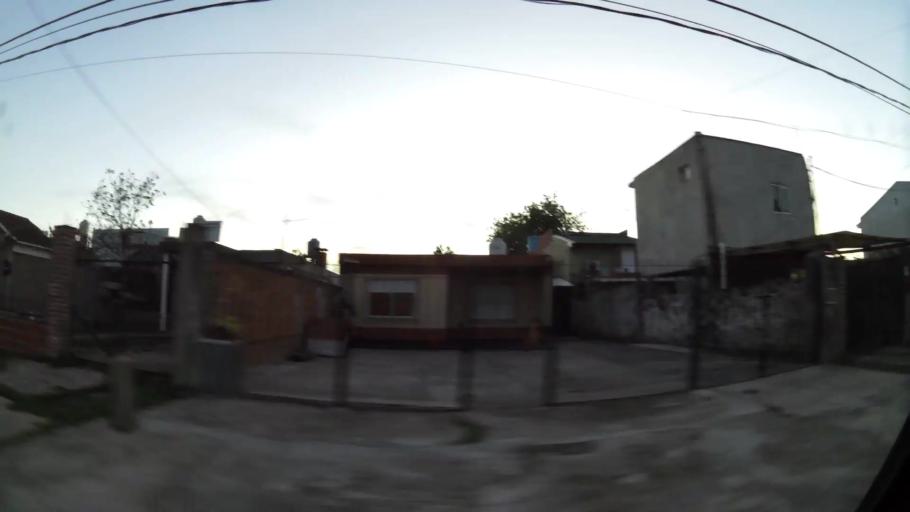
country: AR
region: Buenos Aires
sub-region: Partido de Quilmes
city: Quilmes
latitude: -34.7768
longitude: -58.2155
